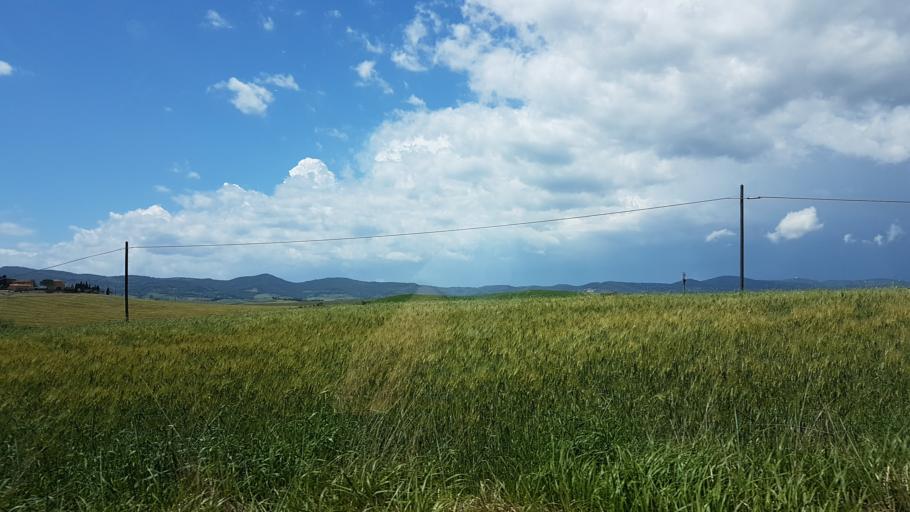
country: IT
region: Tuscany
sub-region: Province of Pisa
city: Orciano Pisano
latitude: 43.4543
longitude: 10.5226
